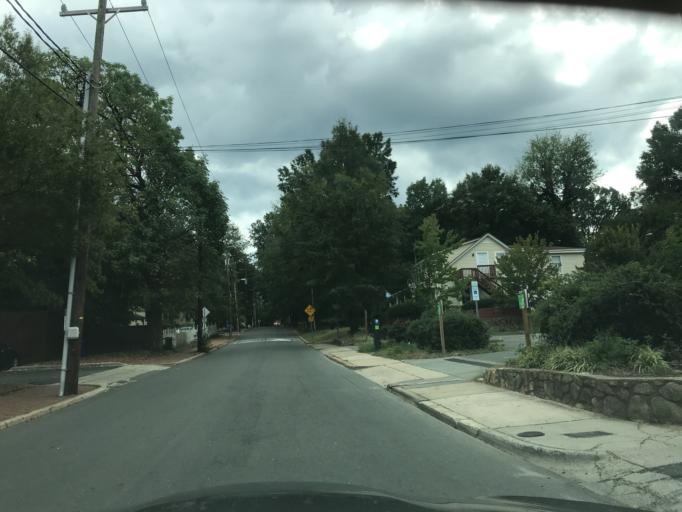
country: US
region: North Carolina
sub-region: Orange County
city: Chapel Hill
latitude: 35.9113
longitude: -79.0593
